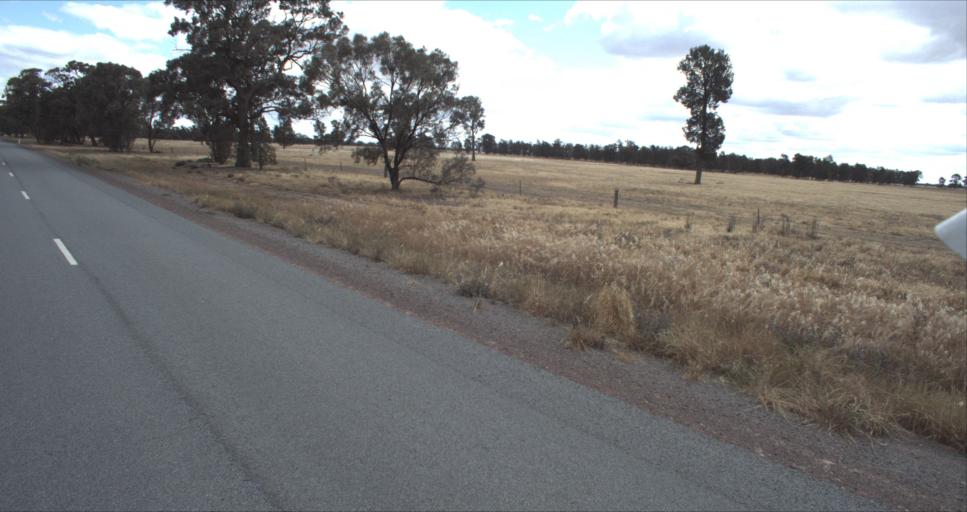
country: AU
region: New South Wales
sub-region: Leeton
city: Leeton
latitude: -34.6822
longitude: 146.3454
